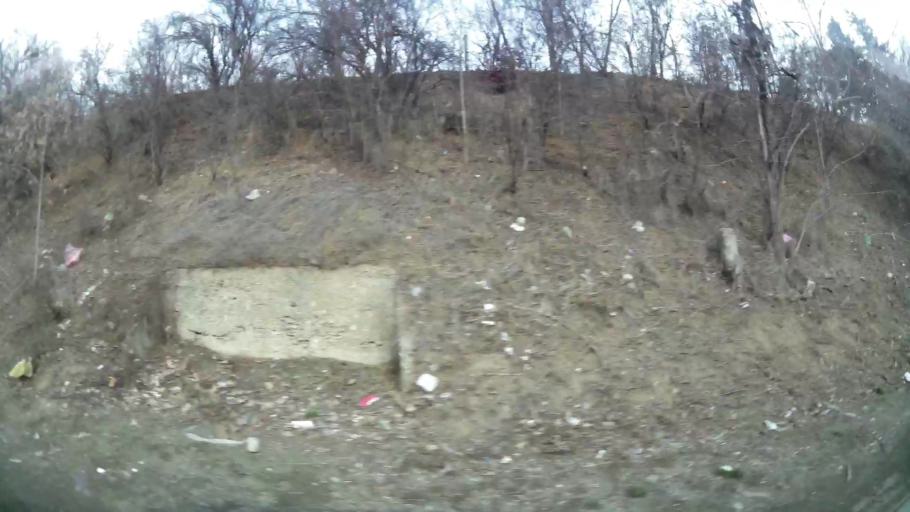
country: MK
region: Cair
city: Cair
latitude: 42.0123
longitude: 21.4254
